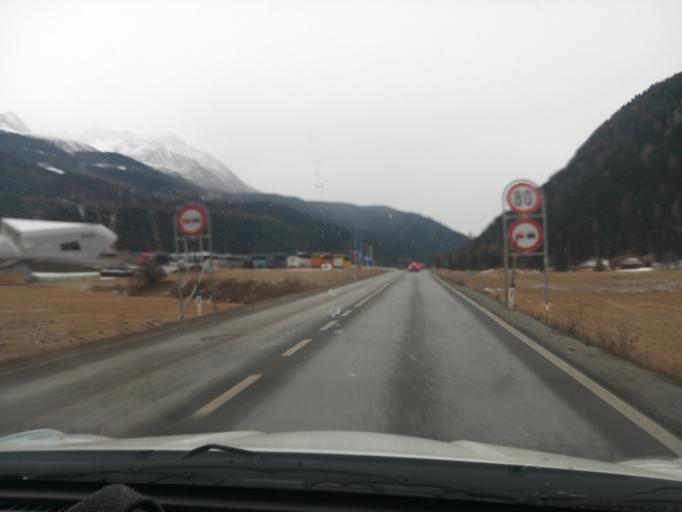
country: AT
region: Tyrol
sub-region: Politischer Bezirk Landeck
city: Nauders
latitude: 46.8771
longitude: 10.5066
